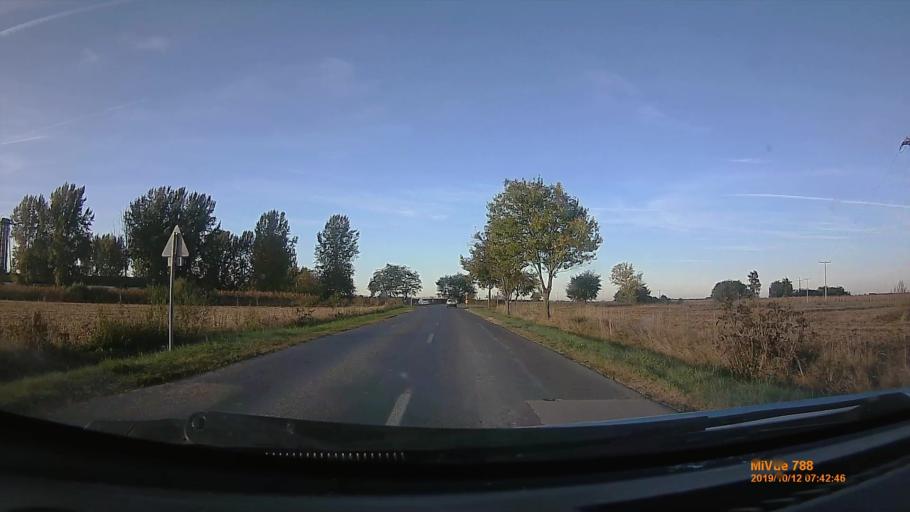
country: RO
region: Bihor
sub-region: Comuna Bors
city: Bors
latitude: 47.1990
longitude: 21.7899
